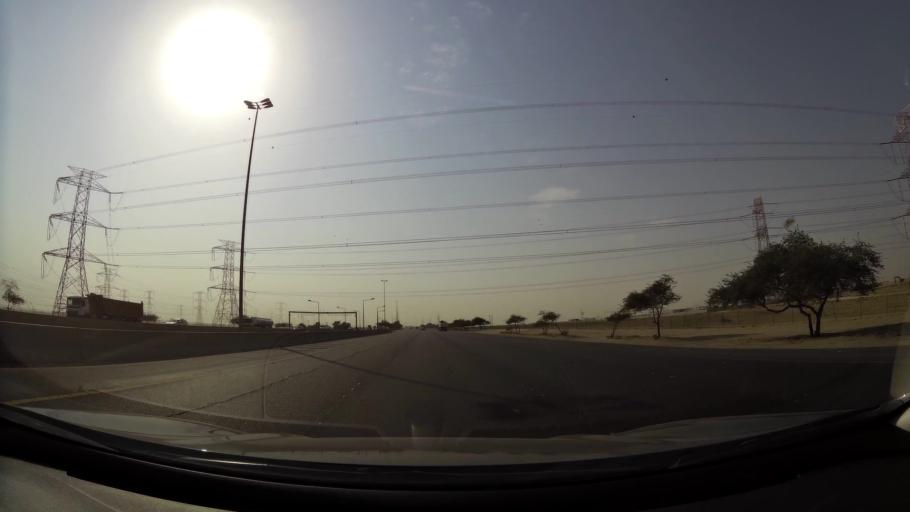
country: KW
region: Al Ahmadi
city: Al Ahmadi
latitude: 29.0040
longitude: 48.0955
